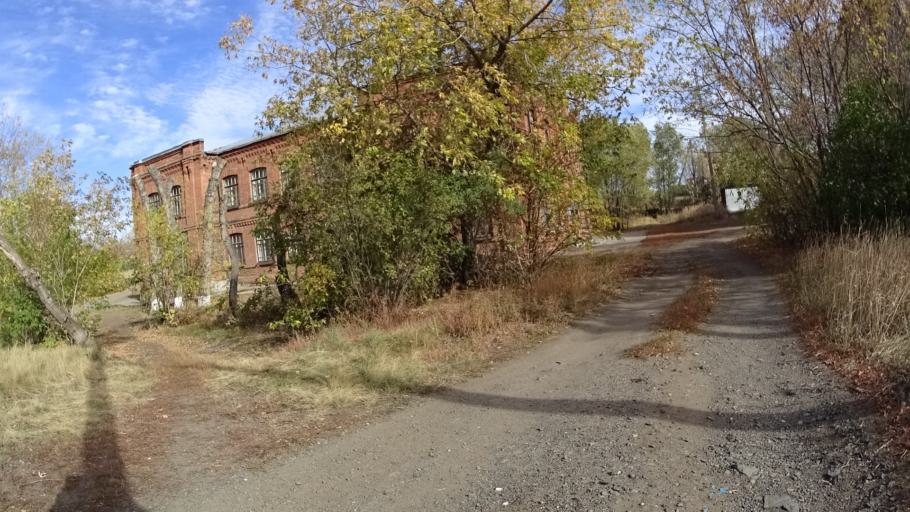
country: RU
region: Chelyabinsk
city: Troitsk
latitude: 54.0785
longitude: 61.5836
